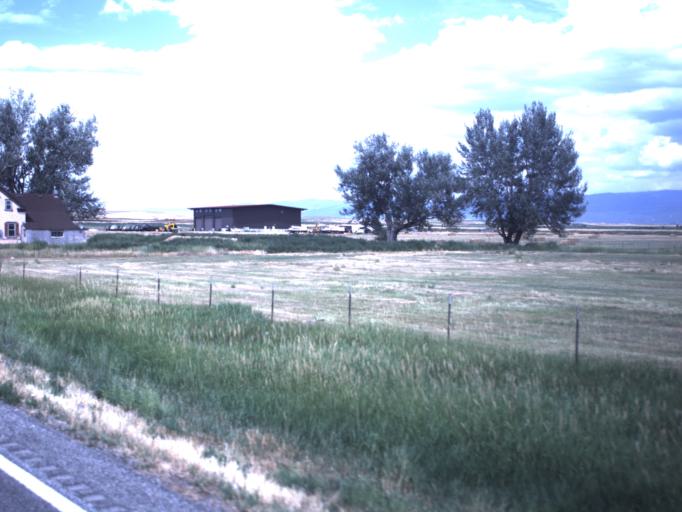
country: US
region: Utah
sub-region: Sanpete County
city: Moroni
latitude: 39.4821
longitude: -111.5630
